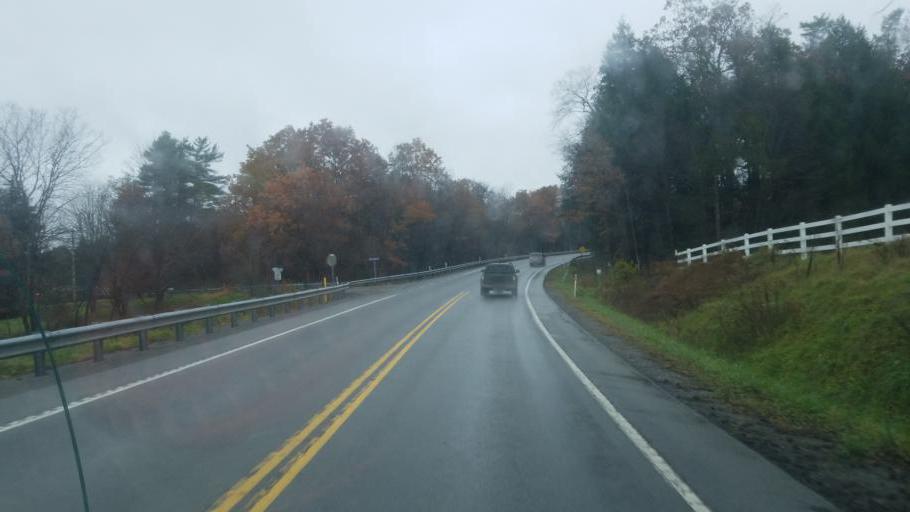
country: US
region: Pennsylvania
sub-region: Clearfield County
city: Shiloh
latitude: 41.1027
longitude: -78.2416
